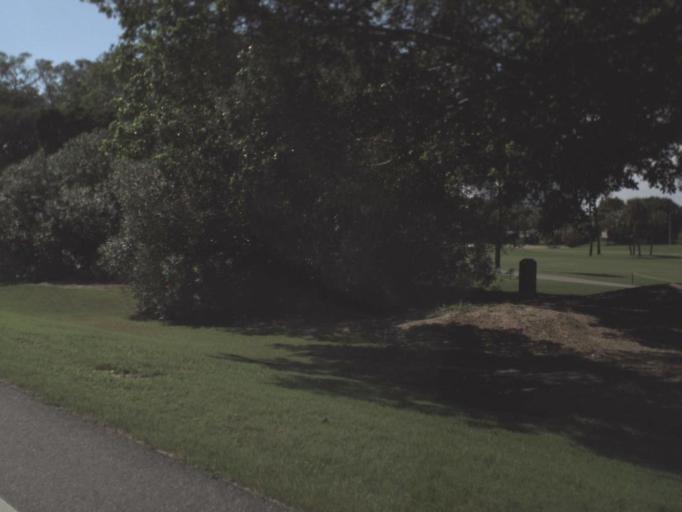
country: US
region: Florida
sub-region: Sarasota County
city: Siesta Key
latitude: 27.3423
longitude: -82.5991
